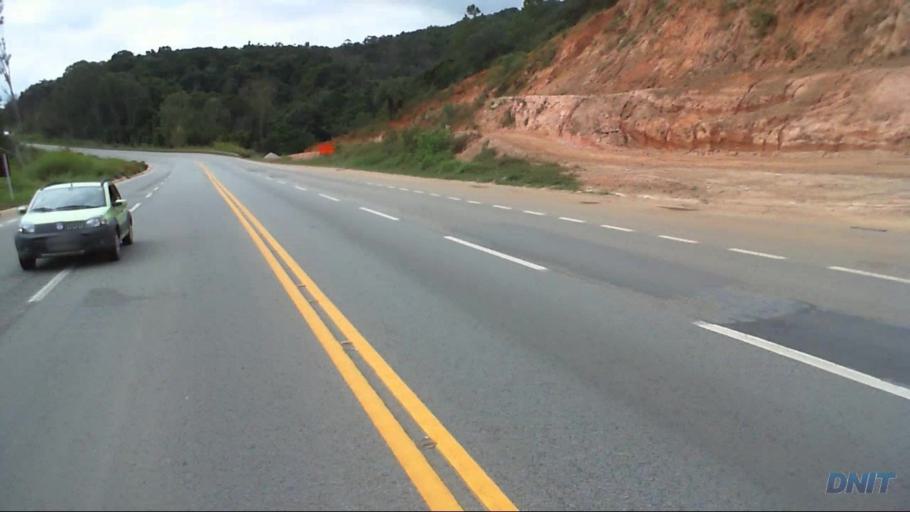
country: BR
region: Minas Gerais
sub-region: Caete
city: Caete
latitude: -19.7748
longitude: -43.6517
